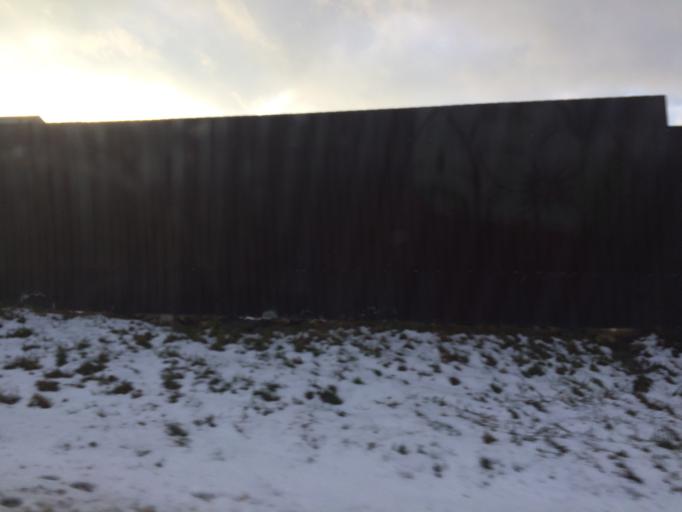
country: RU
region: Tula
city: Cherepet'
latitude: 54.1106
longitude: 36.3275
